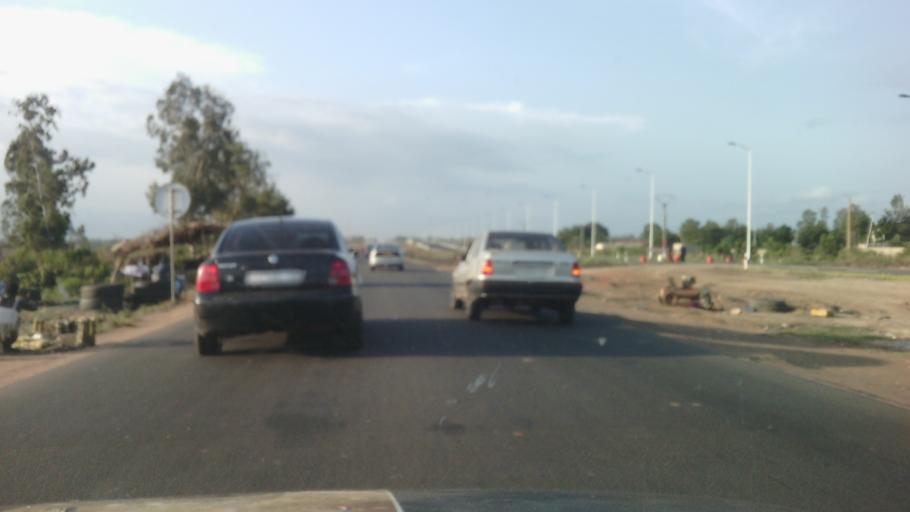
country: TG
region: Maritime
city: Tsevie
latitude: 6.3003
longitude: 1.2142
